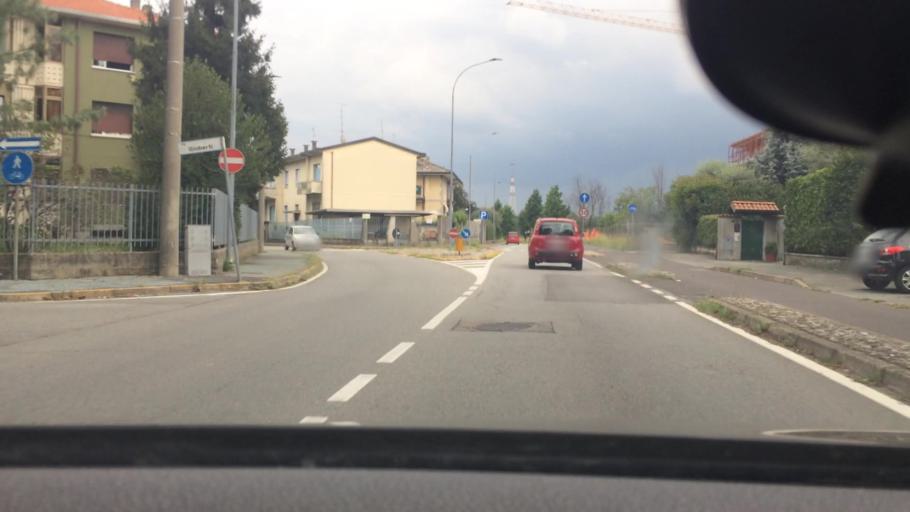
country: IT
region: Lombardy
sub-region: Citta metropolitana di Milano
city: Cerro Maggiore
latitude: 45.5895
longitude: 8.9625
